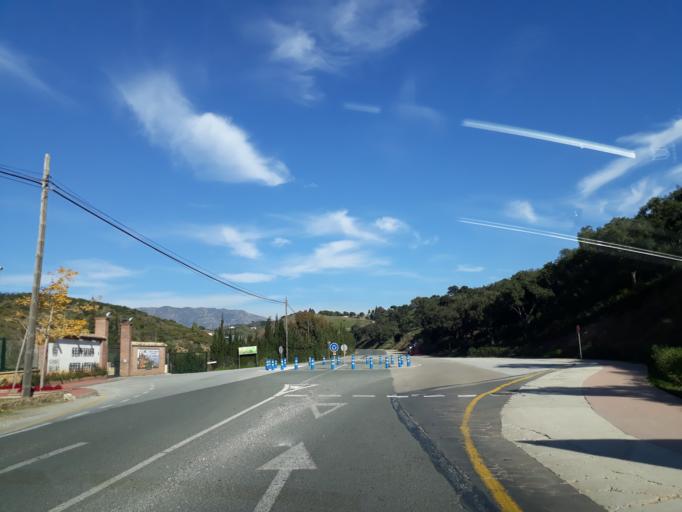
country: ES
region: Andalusia
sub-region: Provincia de Malaga
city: Fuengirola
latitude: 36.5146
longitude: -4.6866
